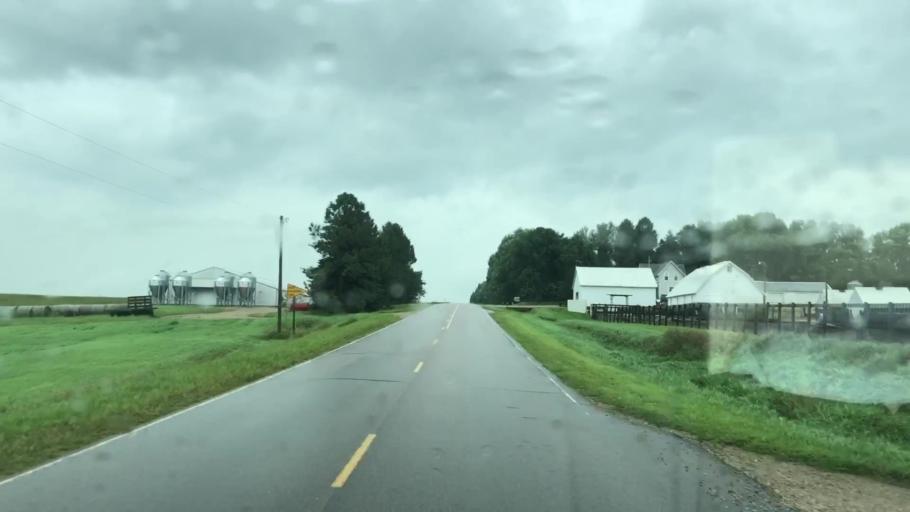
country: US
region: Iowa
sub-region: O'Brien County
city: Sanborn
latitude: 43.2388
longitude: -95.7235
